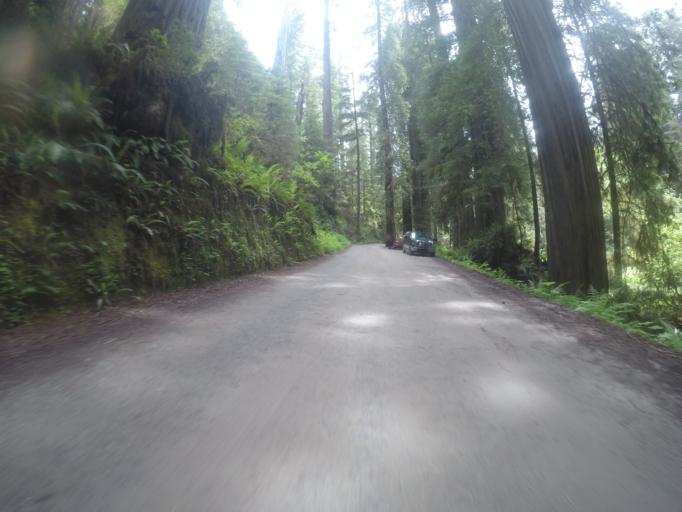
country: US
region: California
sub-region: Del Norte County
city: Bertsch-Oceanview
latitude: 41.7647
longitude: -124.1239
